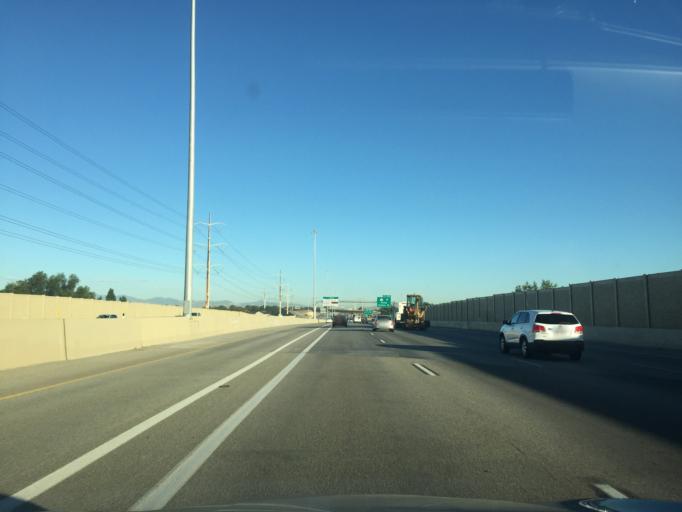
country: US
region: Utah
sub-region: Utah County
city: Provo
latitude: 40.2259
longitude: -111.6768
